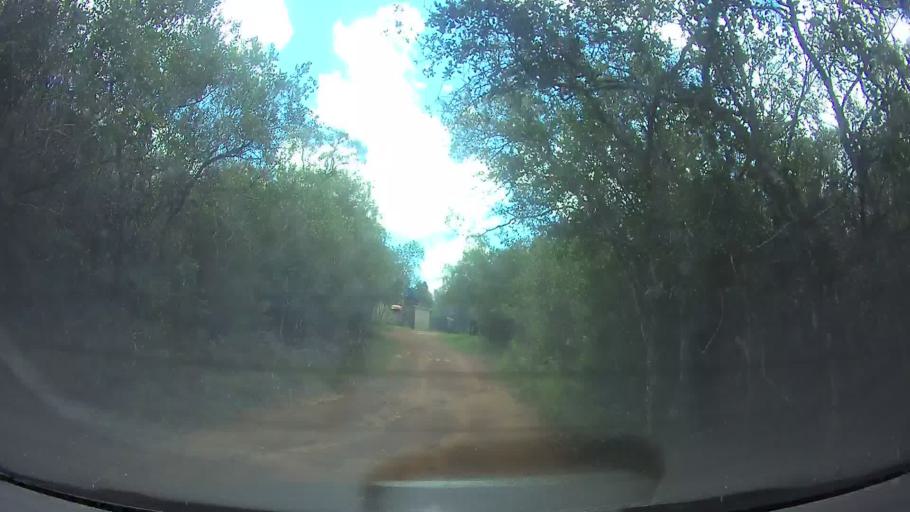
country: PY
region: Paraguari
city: La Colmena
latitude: -25.9741
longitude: -56.7279
